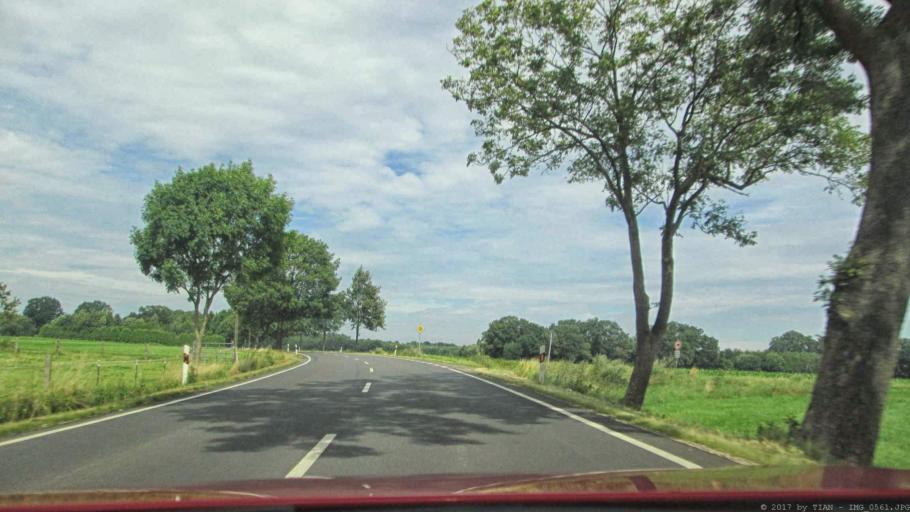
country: DE
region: Saxony-Anhalt
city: Jubar
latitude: 52.6521
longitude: 10.8612
